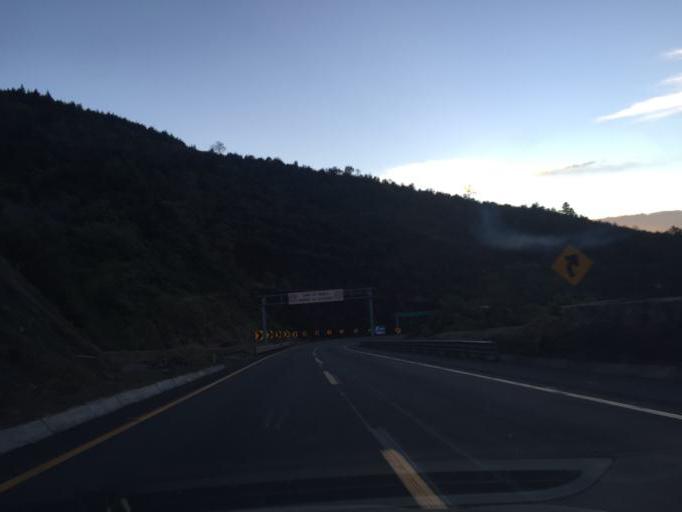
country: MX
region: Veracruz
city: Maltrata
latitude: 18.8284
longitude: -97.2917
